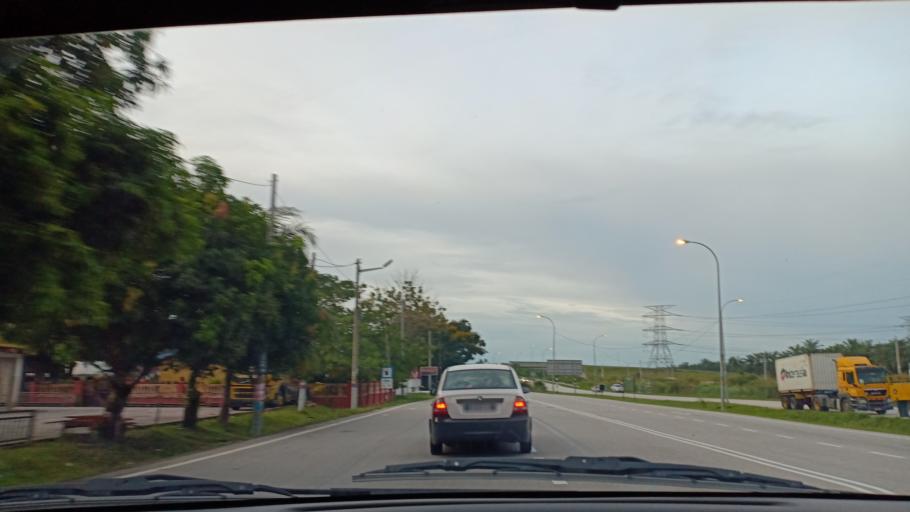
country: MY
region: Penang
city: Tasek Glugor
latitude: 5.5137
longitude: 100.5057
